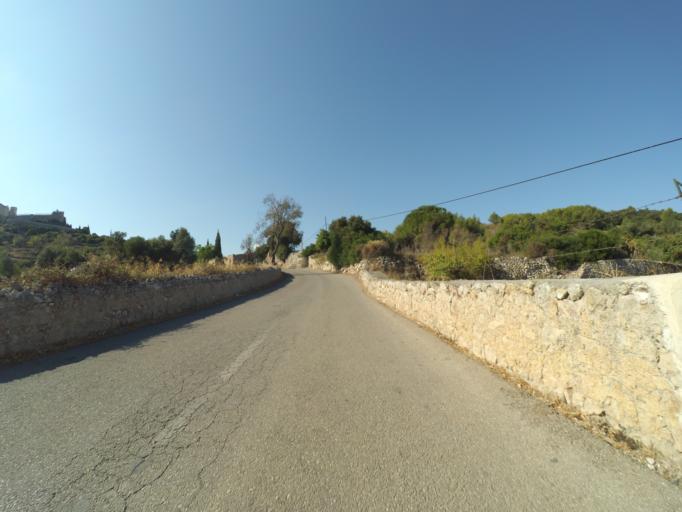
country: ES
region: Balearic Islands
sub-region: Illes Balears
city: Arta
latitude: 39.6989
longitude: 3.3519
